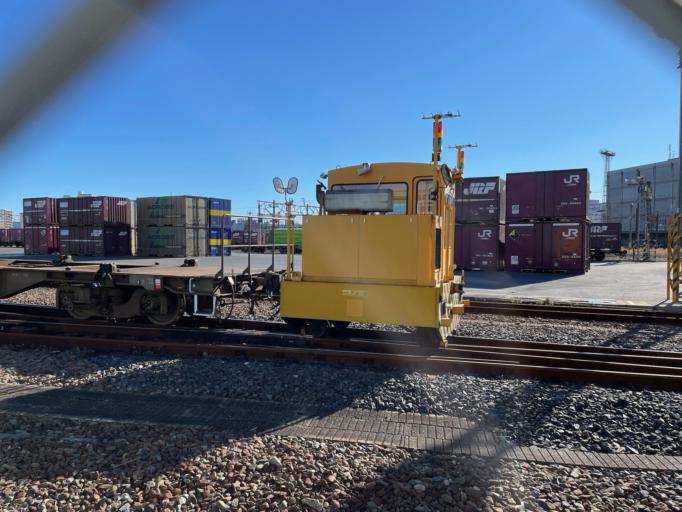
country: JP
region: Saitama
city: Soka
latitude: 35.7329
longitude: 139.8001
